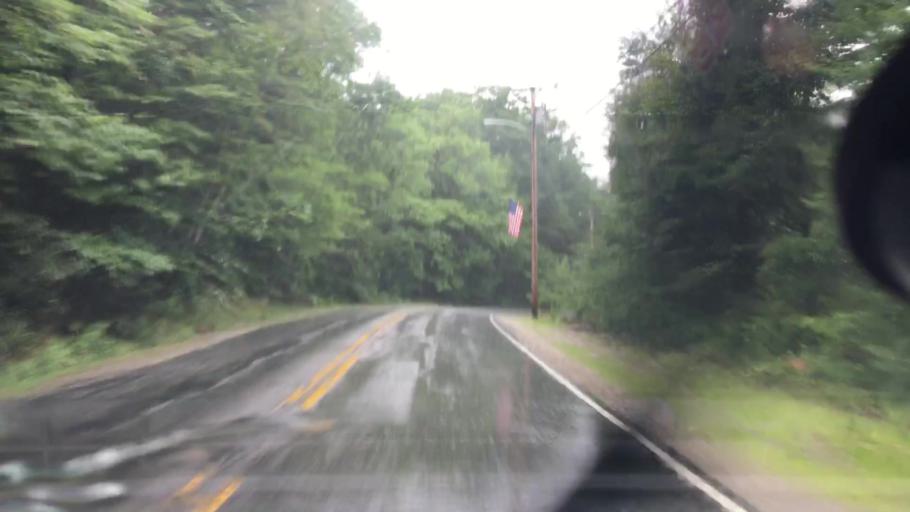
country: US
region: Maine
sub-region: Oxford County
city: Lovell
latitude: 44.2565
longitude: -70.8315
